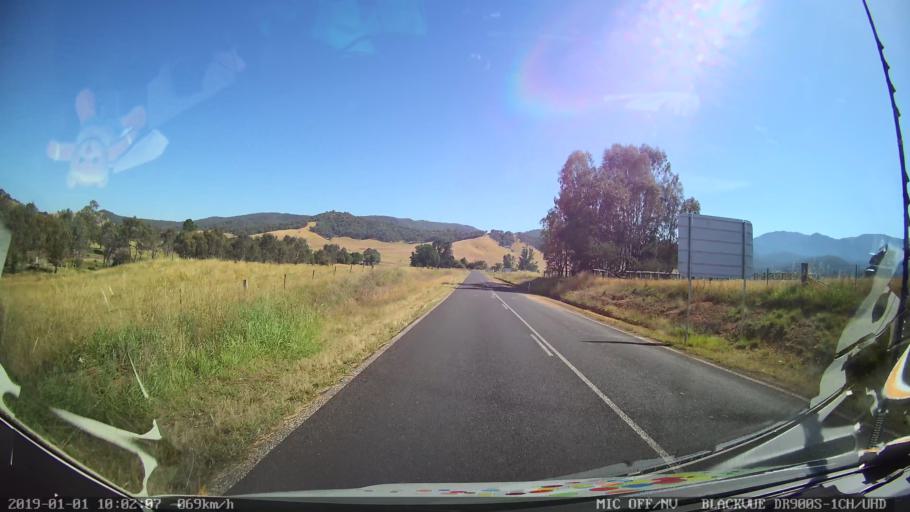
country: AU
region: New South Wales
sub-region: Snowy River
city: Jindabyne
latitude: -36.1845
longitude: 148.1015
